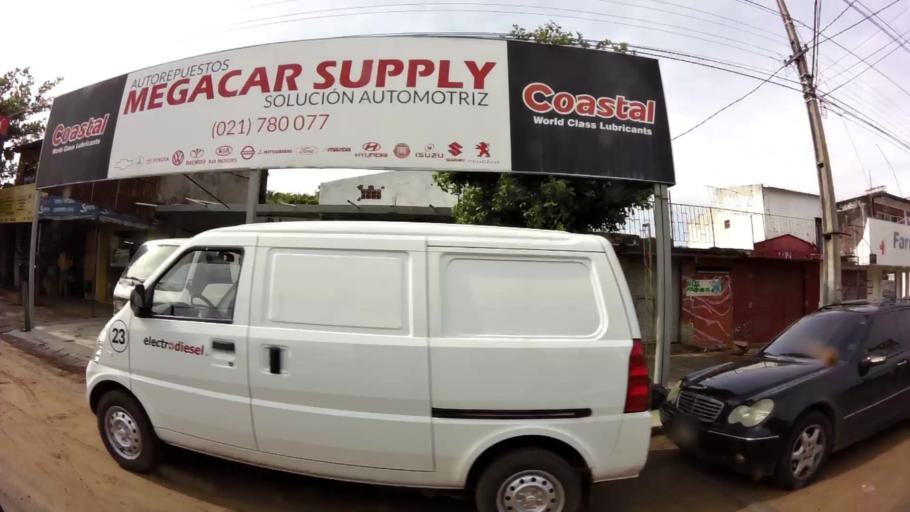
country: PY
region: Central
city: Limpio
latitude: -25.1692
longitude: -57.4774
